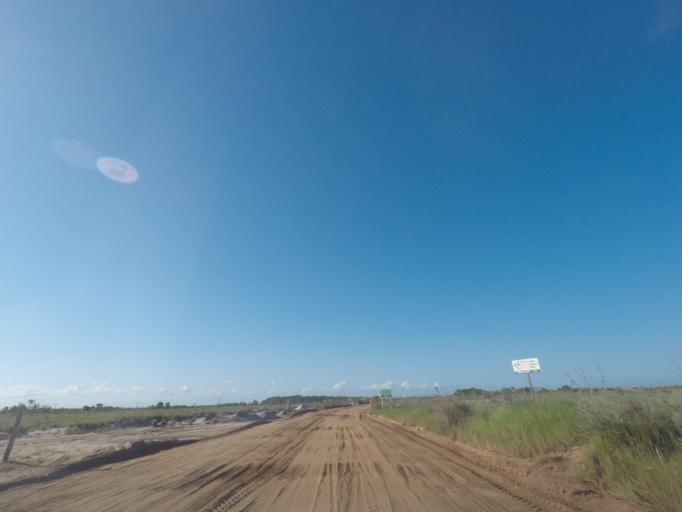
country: BR
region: Bahia
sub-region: Camamu
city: Camamu
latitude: -13.9414
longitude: -38.9455
